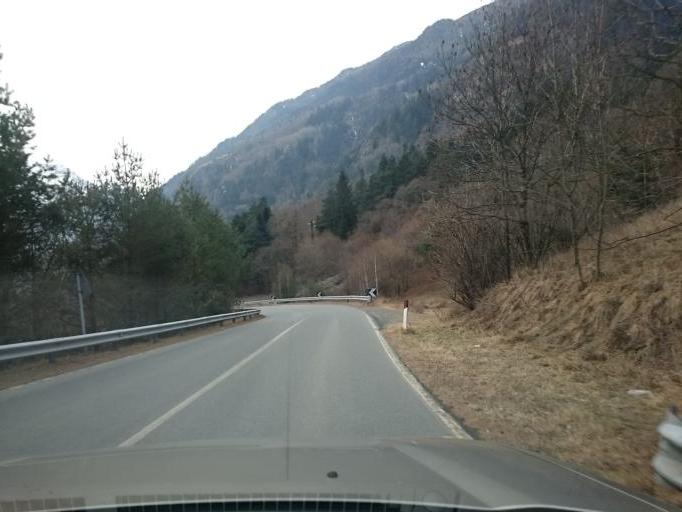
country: IT
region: Lombardy
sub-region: Provincia di Sondrio
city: Sondalo
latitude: 46.3707
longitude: 10.3571
